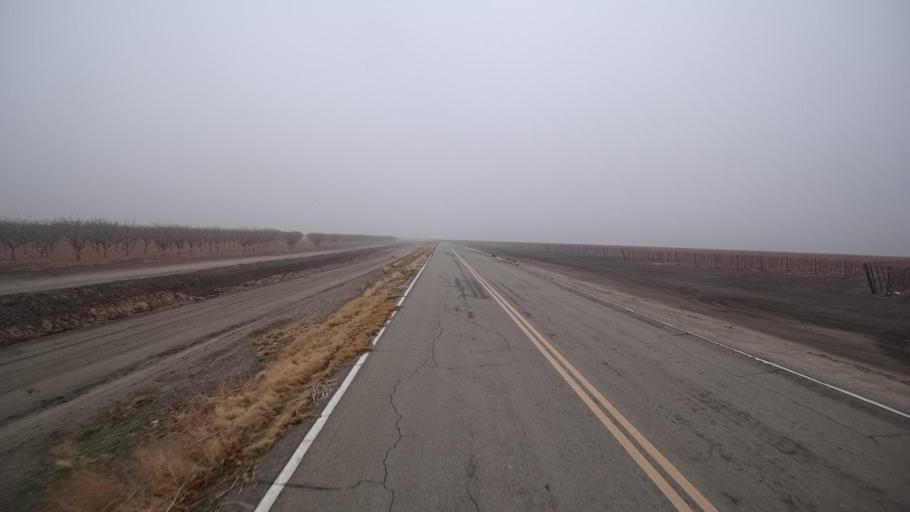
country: US
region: California
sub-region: Kern County
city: Buttonwillow
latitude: 35.4214
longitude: -119.5235
